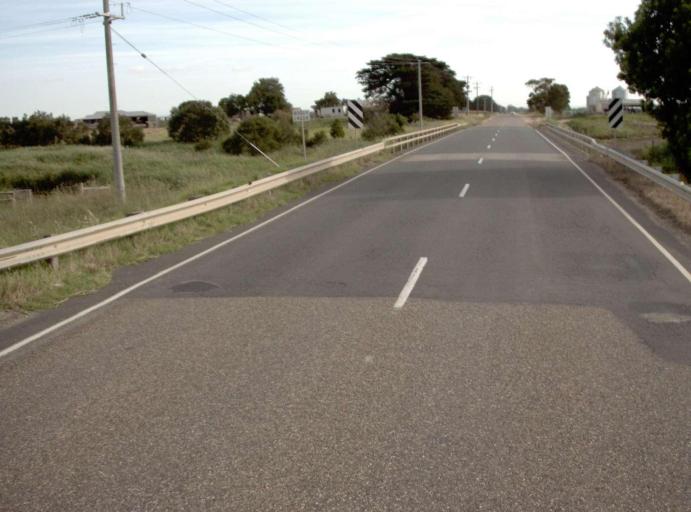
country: AU
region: Victoria
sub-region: Wellington
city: Heyfield
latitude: -37.9819
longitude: 146.8880
